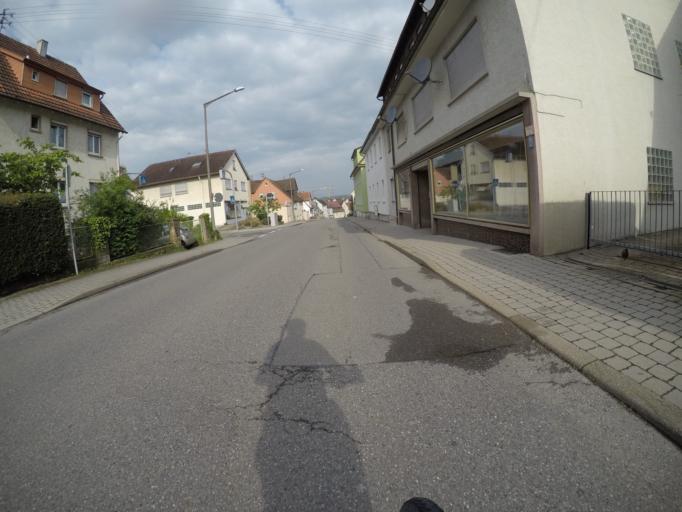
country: DE
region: Baden-Wuerttemberg
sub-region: Regierungsbezirk Stuttgart
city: Magstadt
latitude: 48.7410
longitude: 8.9683
